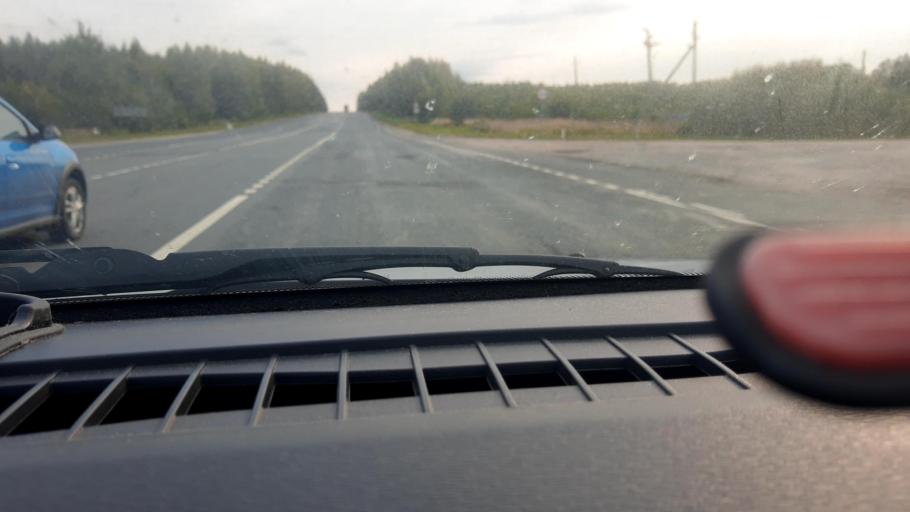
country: RU
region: Nizjnij Novgorod
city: Vladimirskoye
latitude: 56.9719
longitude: 45.1119
